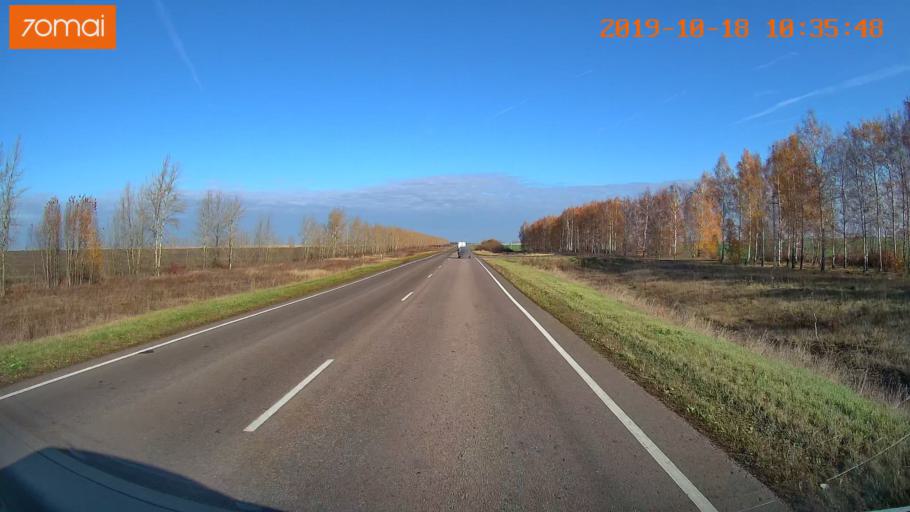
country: RU
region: Tula
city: Kurkino
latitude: 53.5382
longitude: 38.6220
